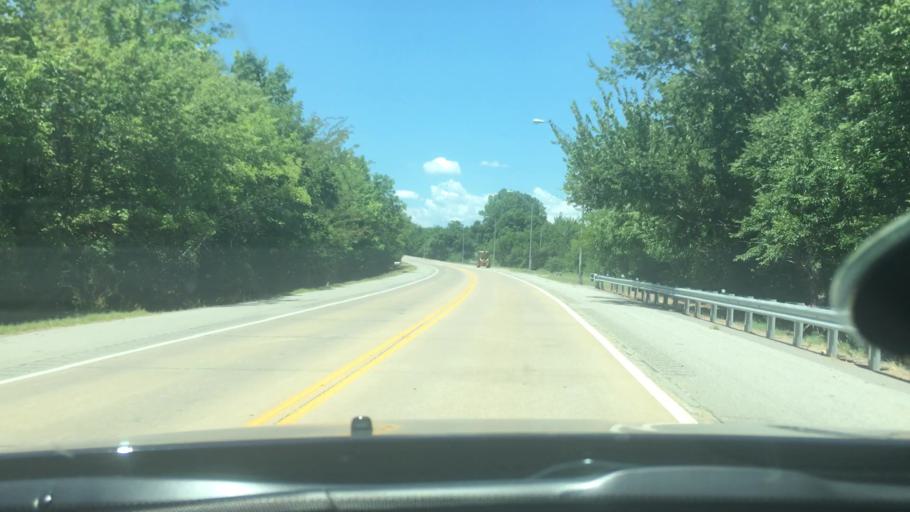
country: US
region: Oklahoma
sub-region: Bryan County
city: Durant
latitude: 34.0159
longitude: -96.1293
